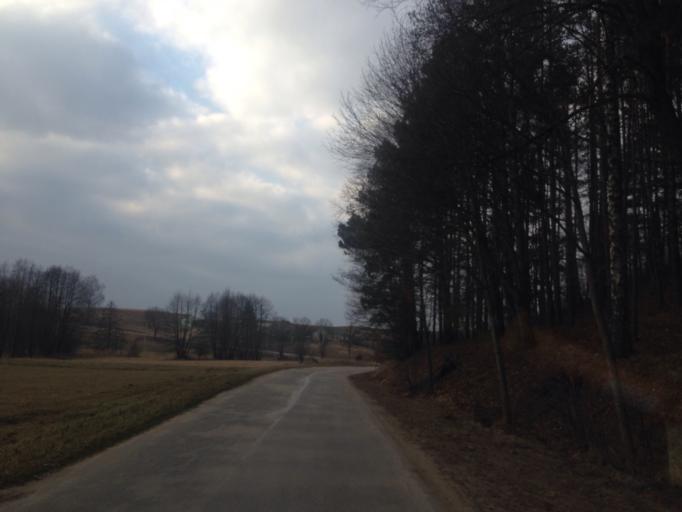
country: PL
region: Kujawsko-Pomorskie
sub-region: Powiat brodnicki
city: Brzozie
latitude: 53.3509
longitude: 19.7267
